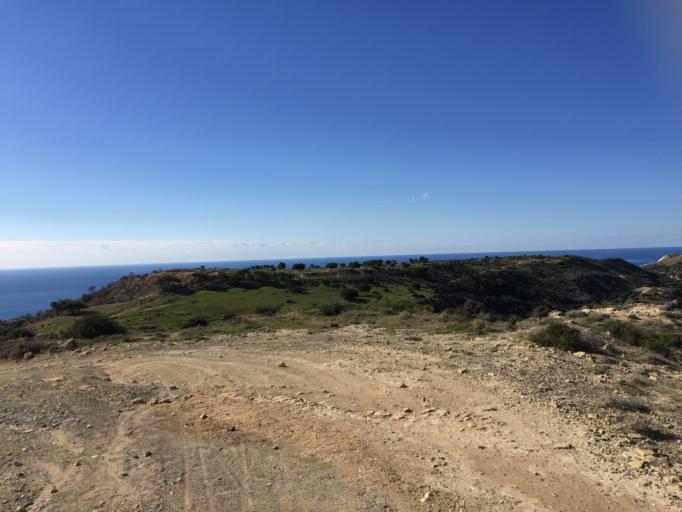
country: CY
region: Limassol
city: Pissouri
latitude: 34.6617
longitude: 32.6777
